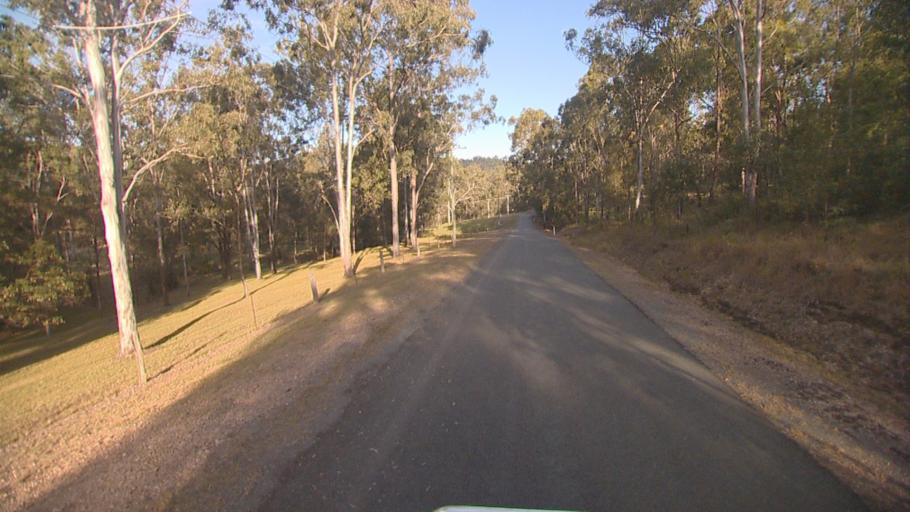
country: AU
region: Queensland
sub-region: Logan
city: Windaroo
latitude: -27.7891
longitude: 153.1761
